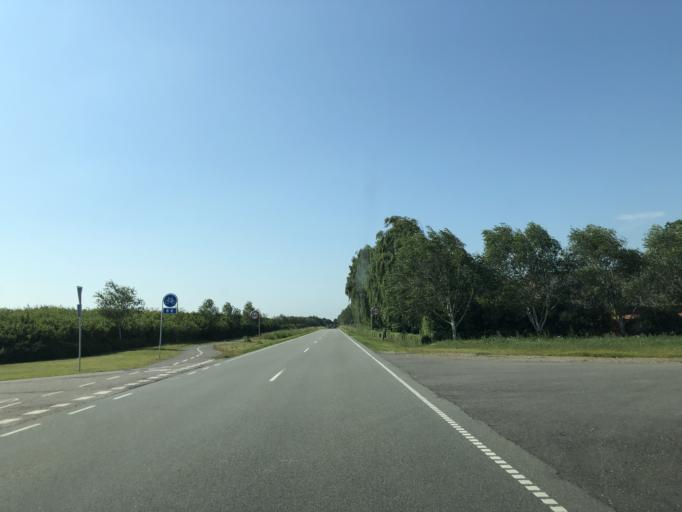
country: DK
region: South Denmark
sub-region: Varde Kommune
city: Varde
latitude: 55.6394
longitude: 8.4860
